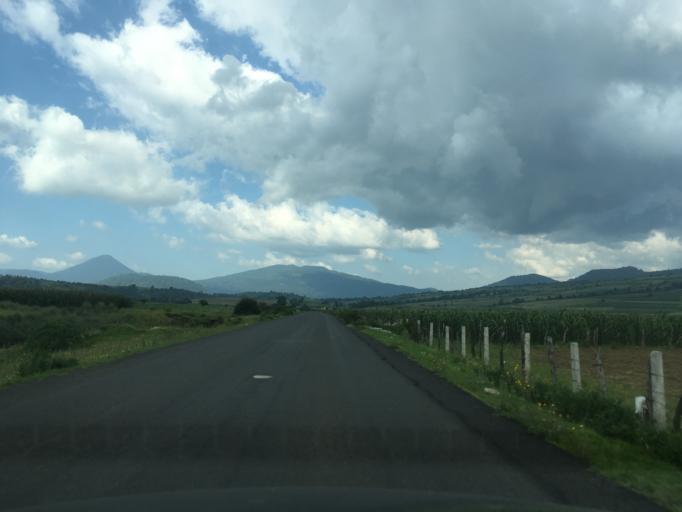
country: MX
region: Michoacan
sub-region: Nahuatzen
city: Comachuen
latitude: 19.6013
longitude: -101.9533
